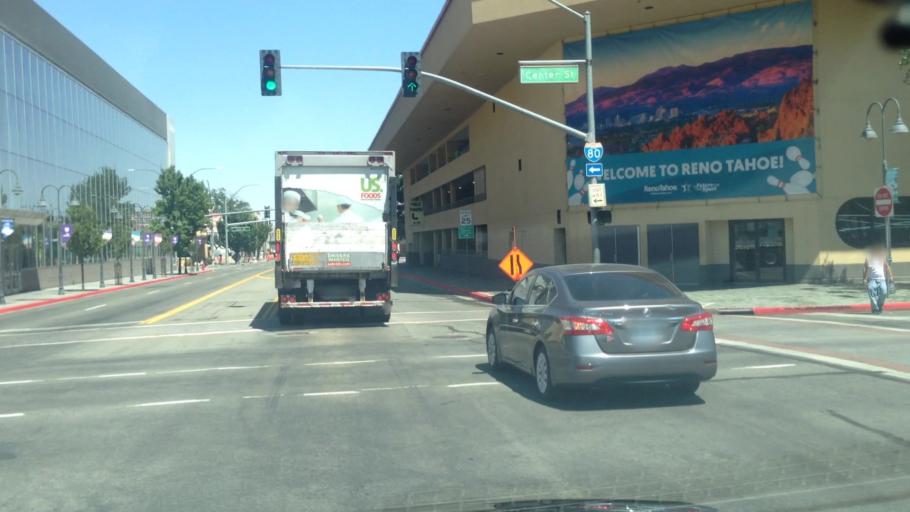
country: US
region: Nevada
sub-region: Washoe County
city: Reno
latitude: 39.5301
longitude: -119.8132
